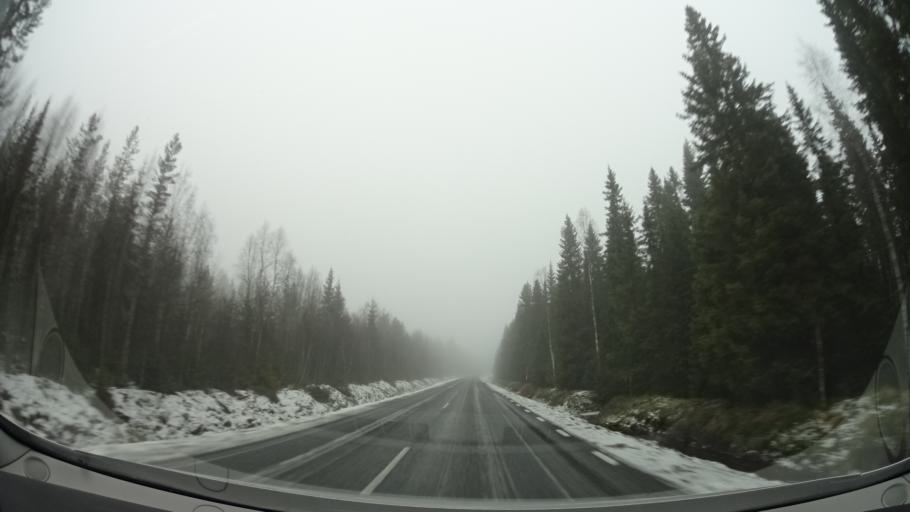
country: SE
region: Vaesterbotten
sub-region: Asele Kommun
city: Insjon
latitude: 64.2679
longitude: 17.5724
